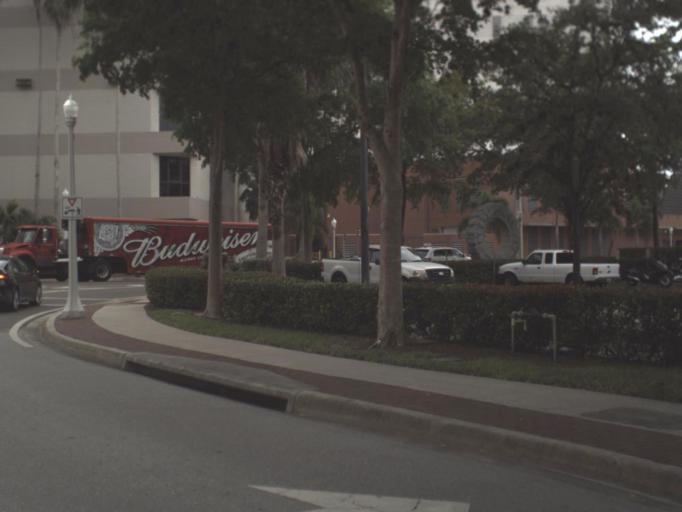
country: US
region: Florida
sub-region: Lee County
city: North Fort Myers
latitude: 26.6428
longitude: -81.8713
